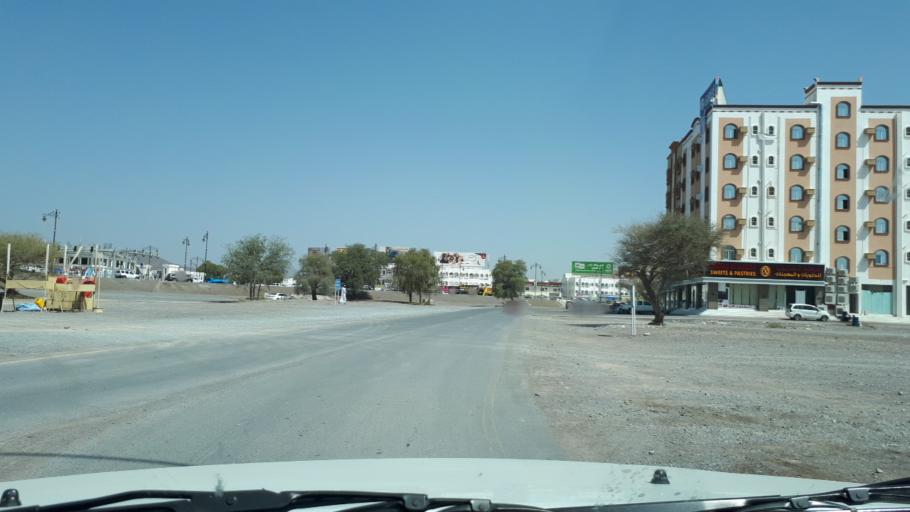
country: OM
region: Muhafazat ad Dakhiliyah
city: Nizwa
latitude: 22.8746
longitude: 57.5352
